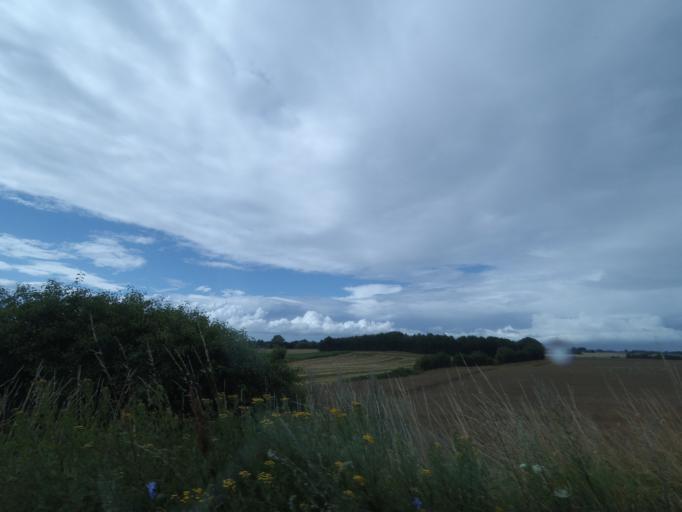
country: DK
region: South Denmark
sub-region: Nordfyns Kommune
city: Sonderso
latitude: 55.4670
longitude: 10.2035
